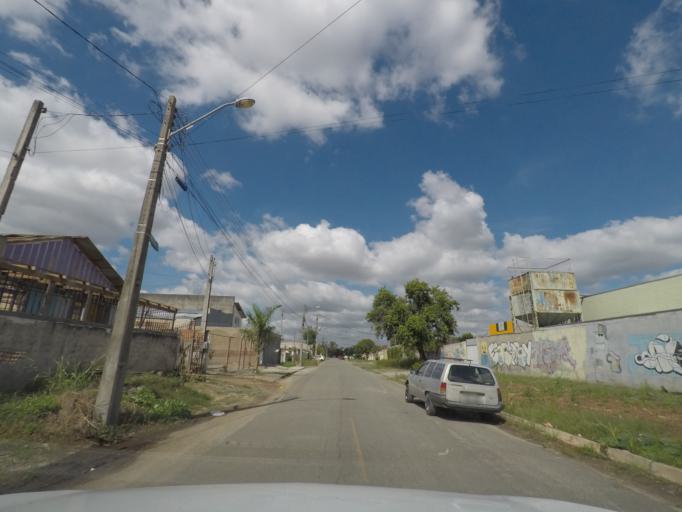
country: BR
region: Parana
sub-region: Sao Jose Dos Pinhais
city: Sao Jose dos Pinhais
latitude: -25.5062
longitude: -49.2167
